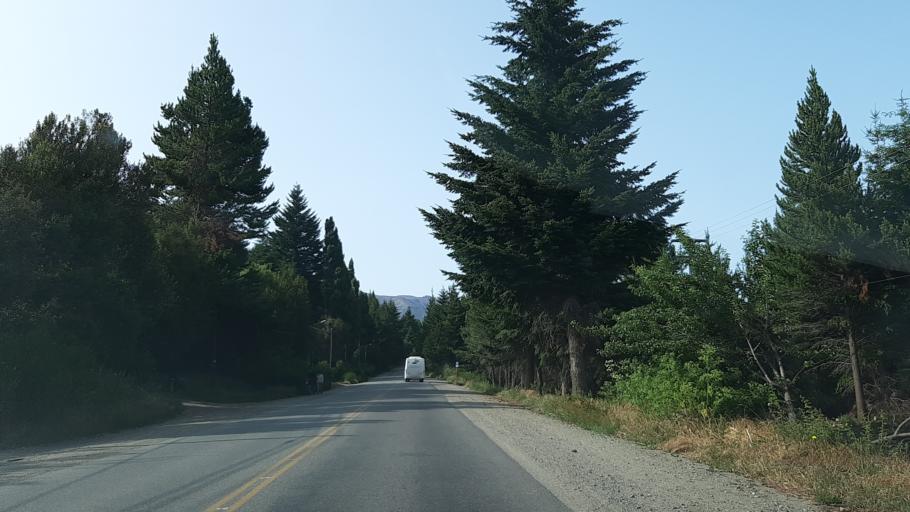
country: AR
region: Rio Negro
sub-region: Departamento de Bariloche
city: San Carlos de Bariloche
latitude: -41.1544
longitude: -71.4084
